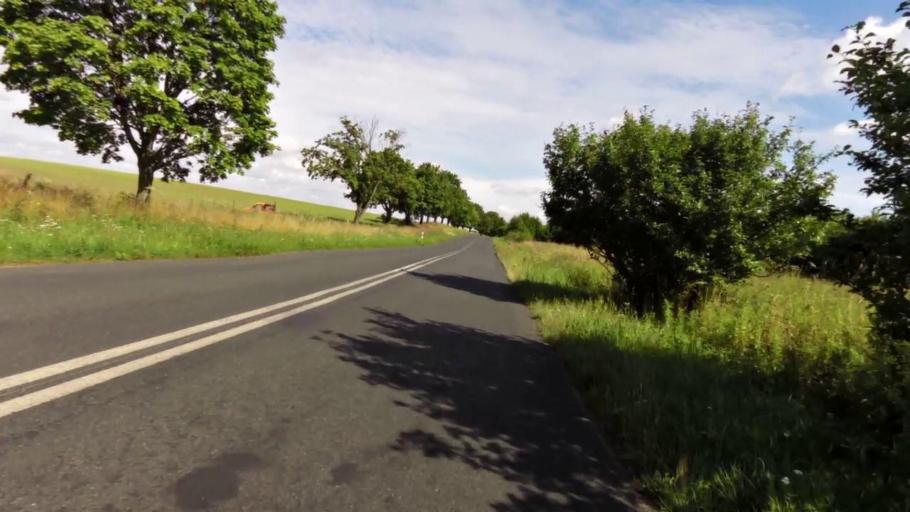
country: PL
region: West Pomeranian Voivodeship
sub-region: Powiat stargardzki
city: Dobrzany
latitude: 53.3950
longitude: 15.4312
